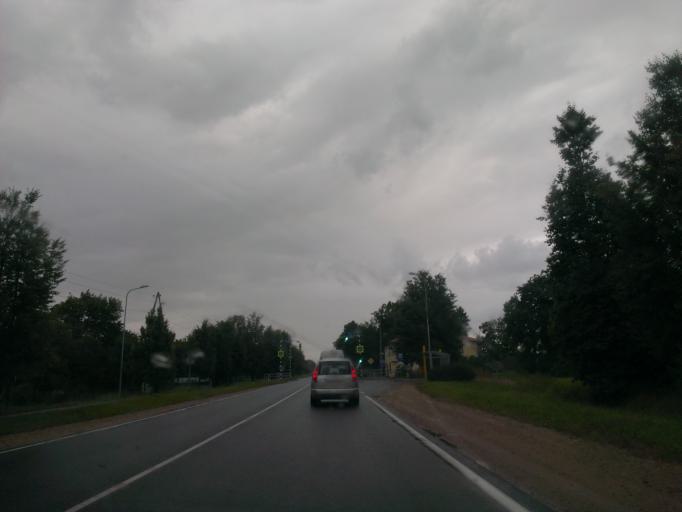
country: LV
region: Ogre
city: Ogre
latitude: 56.7798
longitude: 24.6526
